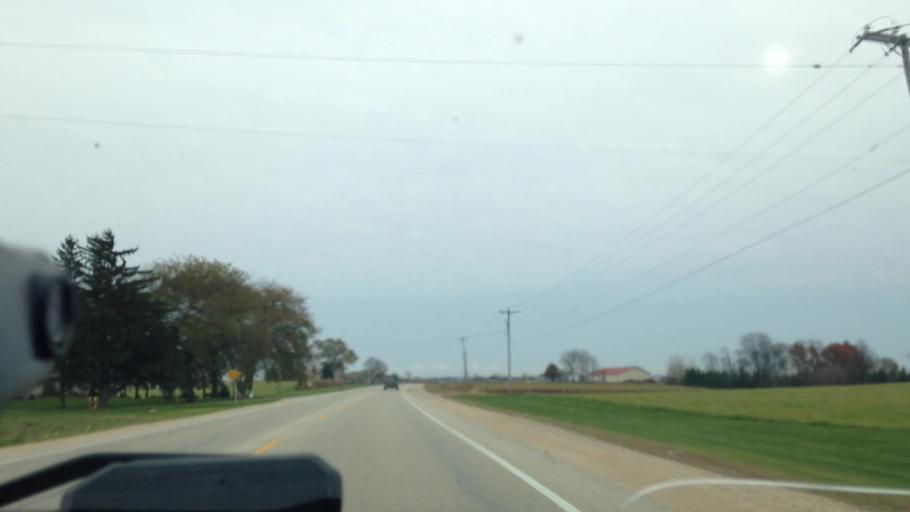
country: US
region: Wisconsin
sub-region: Dodge County
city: Theresa
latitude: 43.4247
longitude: -88.4197
